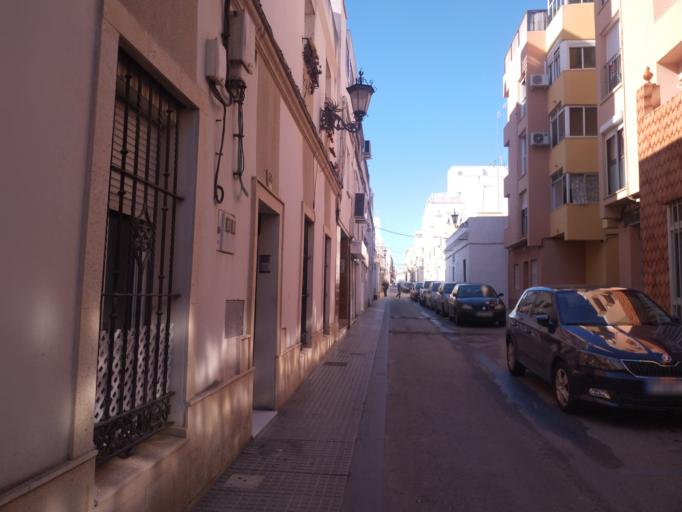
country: ES
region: Andalusia
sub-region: Provincia de Cadiz
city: San Fernando
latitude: 36.4710
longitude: -6.1930
